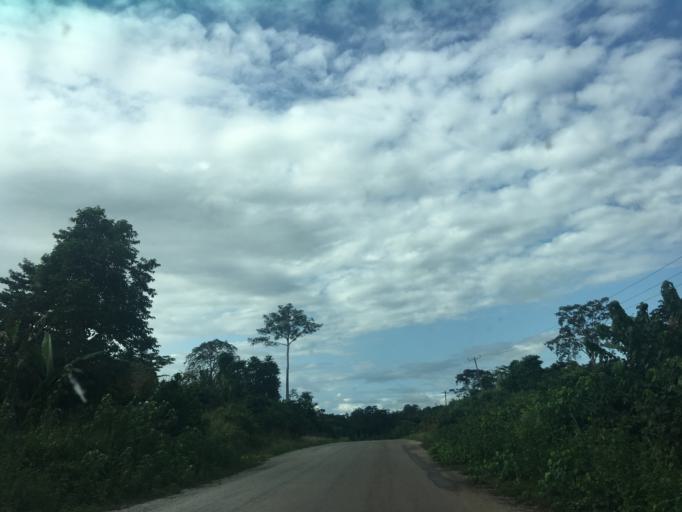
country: GH
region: Western
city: Wassa-Akropong
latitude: 6.0100
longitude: -2.4054
